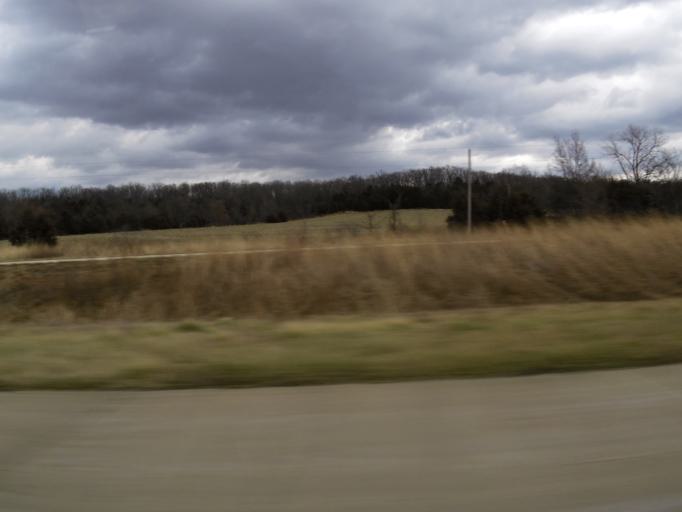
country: US
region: Missouri
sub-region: Pike County
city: Bowling Green
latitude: 39.4477
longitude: -91.2664
